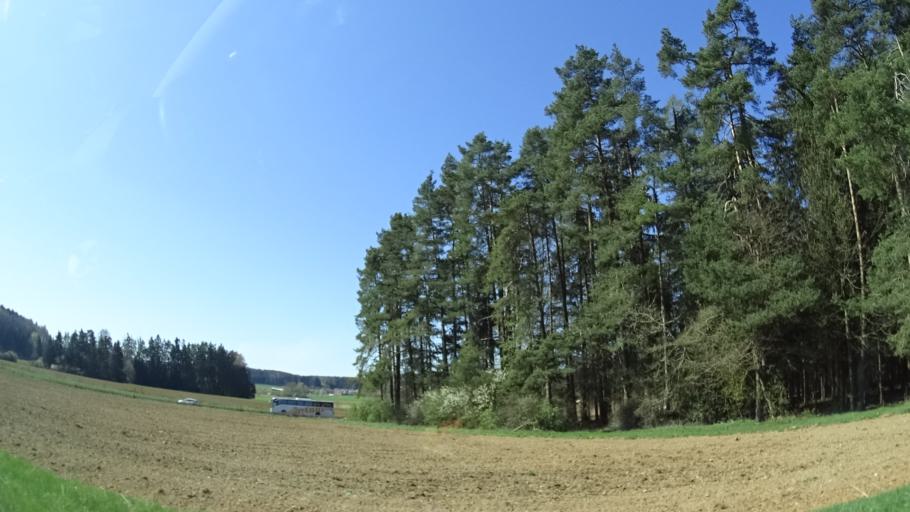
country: DE
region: Bavaria
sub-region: Regierungsbezirk Mittelfranken
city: Alfeld
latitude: 49.4140
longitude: 11.5671
